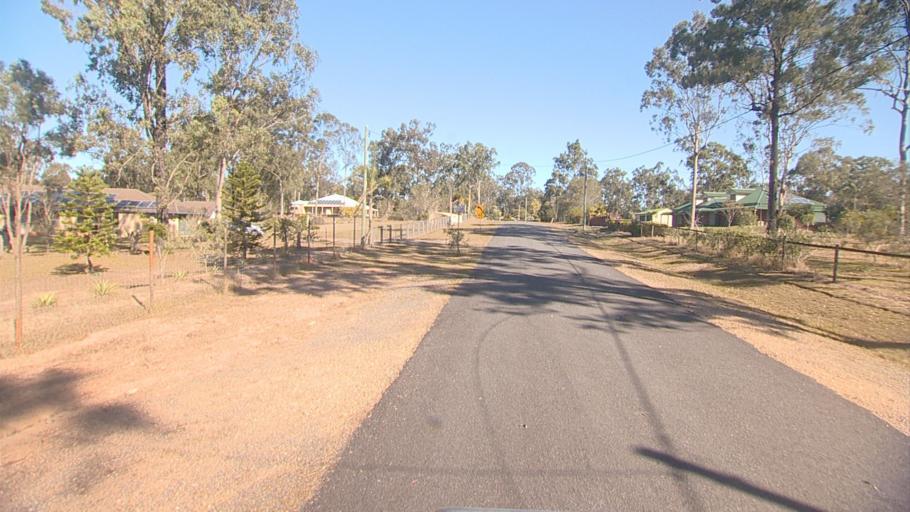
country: AU
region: Queensland
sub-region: Ipswich
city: Springfield Lakes
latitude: -27.7257
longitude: 152.9599
